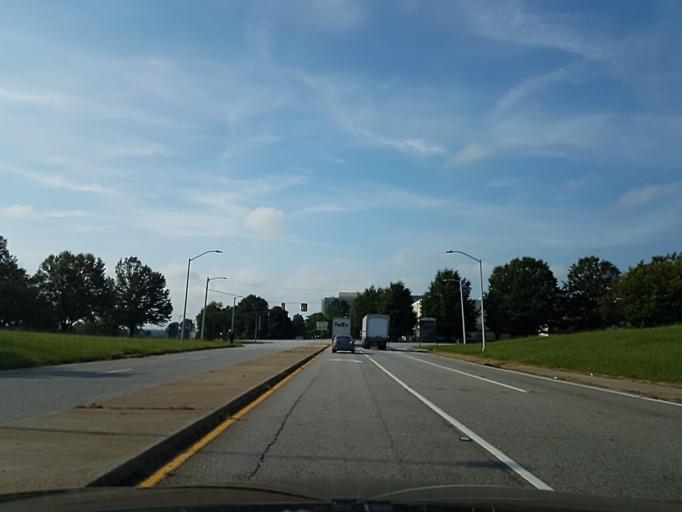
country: US
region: Georgia
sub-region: Fulton County
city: Hapeville
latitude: 33.6584
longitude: -84.4270
